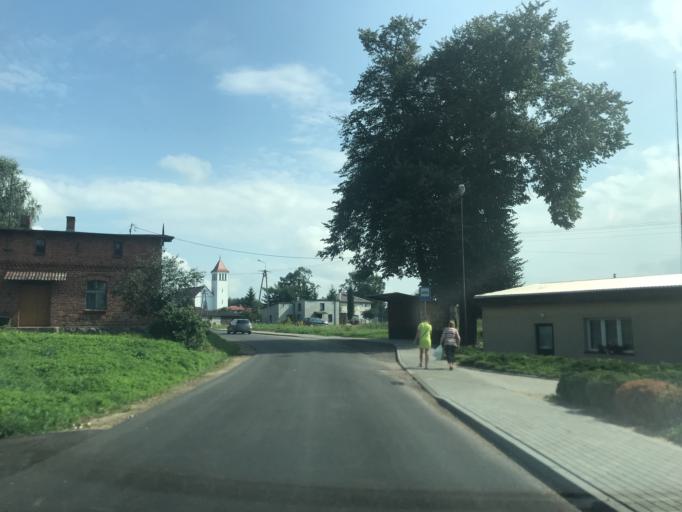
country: PL
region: Warmian-Masurian Voivodeship
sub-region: Powiat nowomiejski
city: Kurzetnik
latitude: 53.3831
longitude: 19.4659
